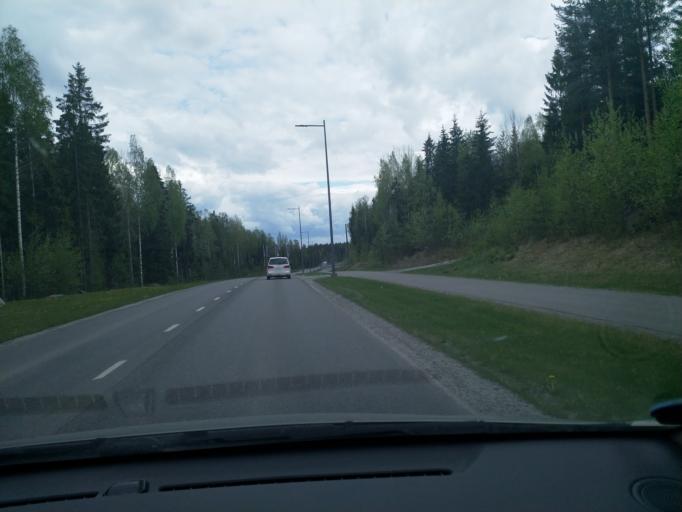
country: FI
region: Pirkanmaa
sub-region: Tampere
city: Tampere
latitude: 61.4525
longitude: 23.8006
